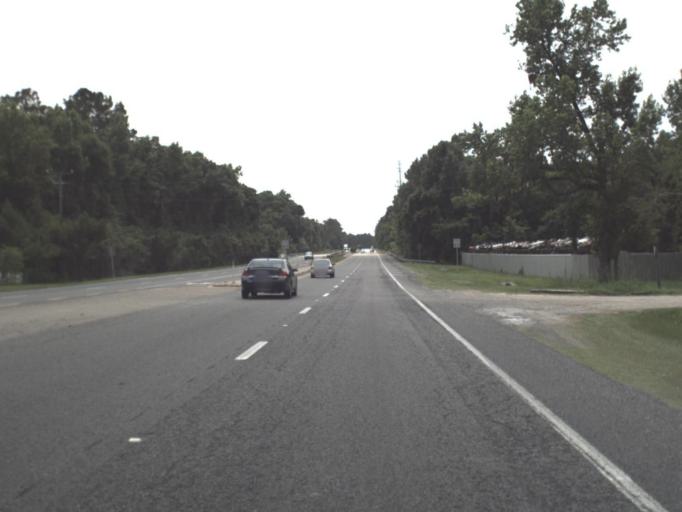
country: US
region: Florida
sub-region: Nassau County
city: Nassau Village-Ratliff
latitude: 30.5085
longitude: -81.7926
